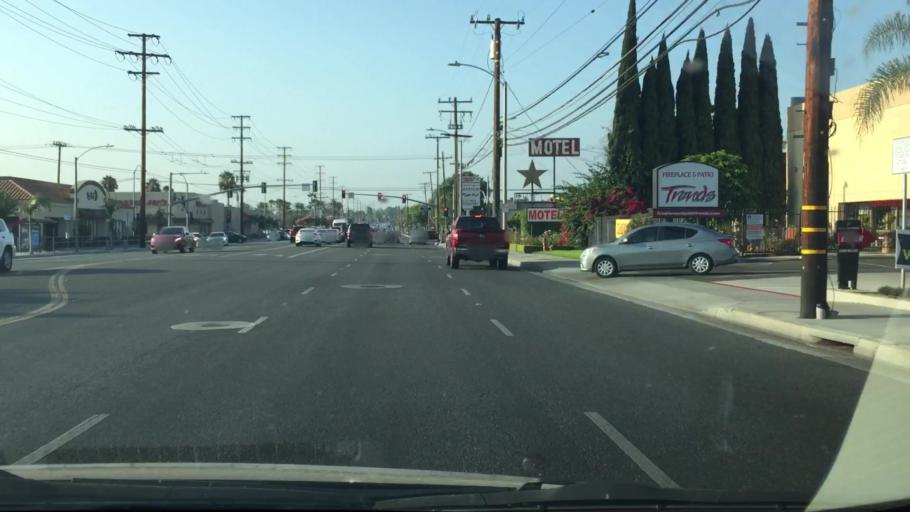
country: US
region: California
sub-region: Orange County
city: Villa Park
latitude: 33.8218
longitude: -117.8359
